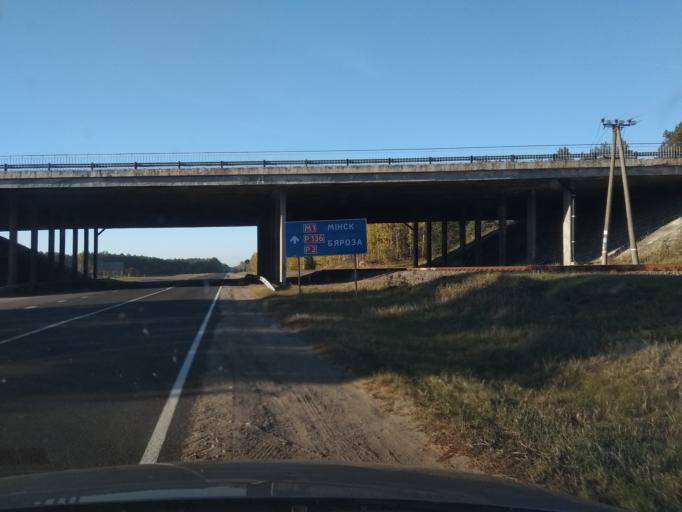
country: BY
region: Brest
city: Nyakhachava
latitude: 52.5755
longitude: 25.1118
